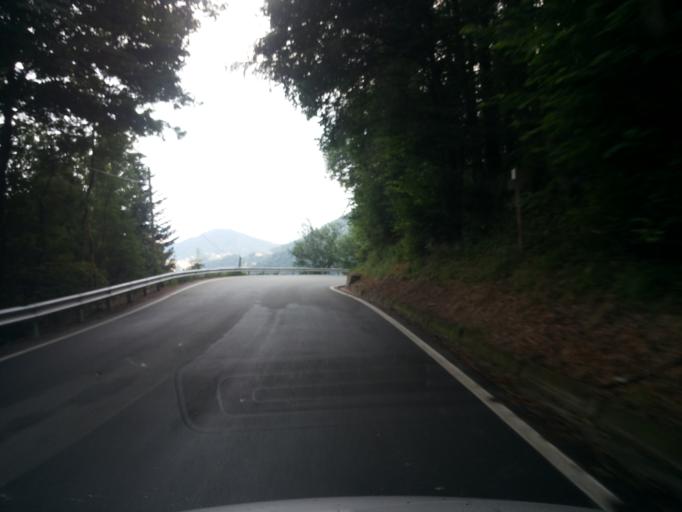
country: IT
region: Piedmont
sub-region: Provincia di Biella
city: Pollone
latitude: 45.6155
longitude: 7.9863
